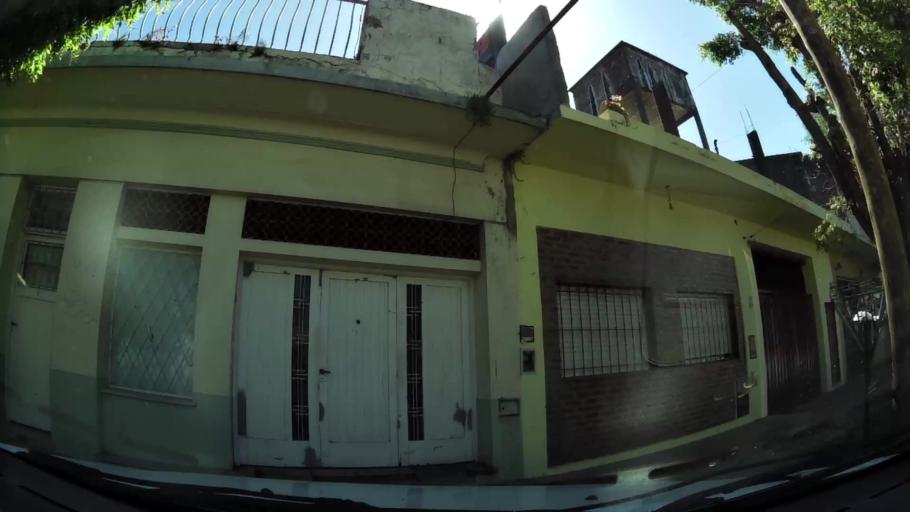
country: AR
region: Buenos Aires
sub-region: Partido de General San Martin
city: General San Martin
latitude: -34.5386
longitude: -58.5753
